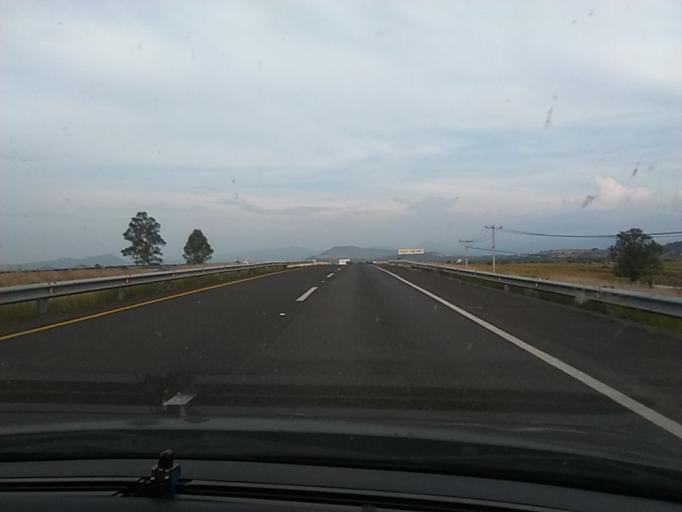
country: MX
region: Michoacan
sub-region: Alvaro Obregon
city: Tzintzimeo
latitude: 19.8908
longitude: -100.9775
